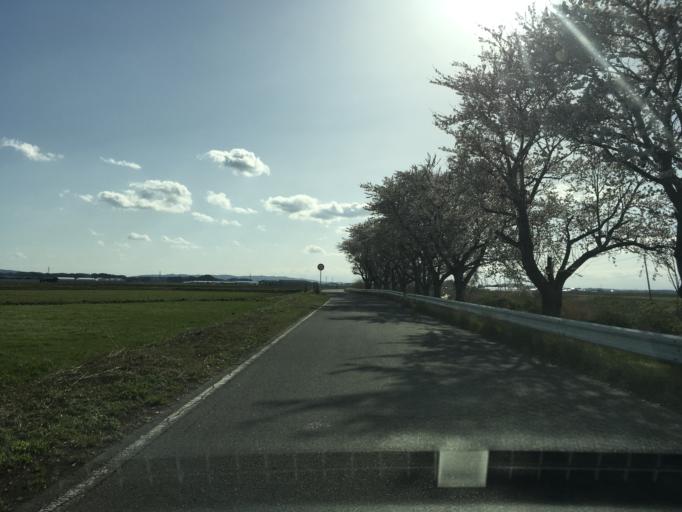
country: JP
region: Miyagi
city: Wakuya
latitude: 38.6651
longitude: 141.2497
